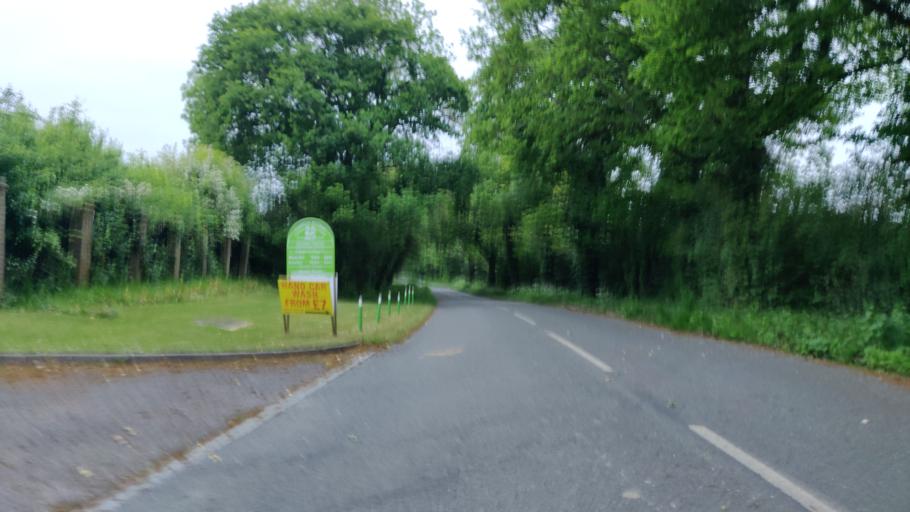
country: GB
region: England
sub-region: West Sussex
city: Partridge Green
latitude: 50.9891
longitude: -0.3038
